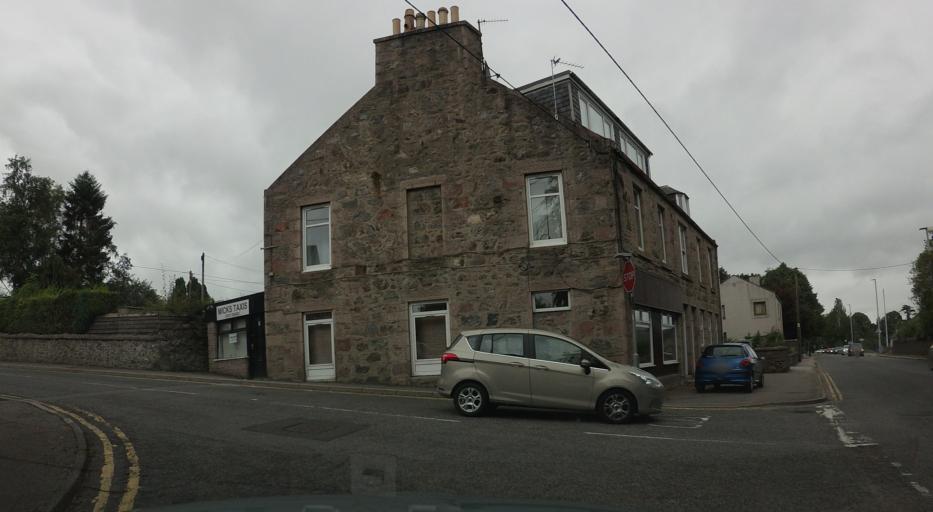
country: GB
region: Scotland
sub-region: Aberdeenshire
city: Banchory
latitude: 57.0513
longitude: -2.4926
